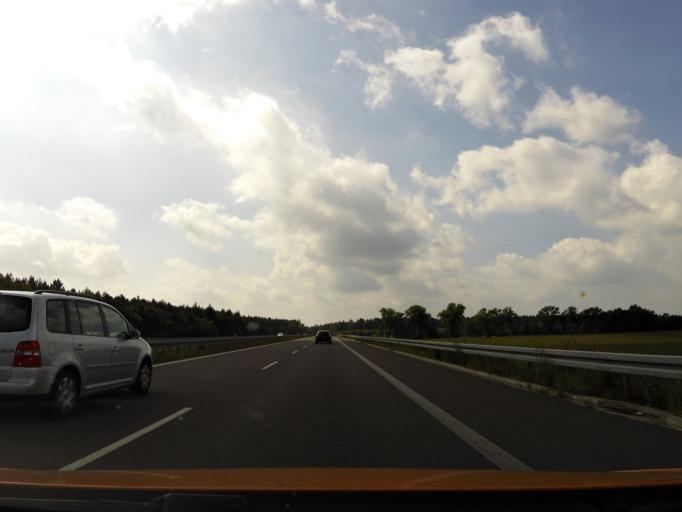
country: PL
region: West Pomeranian Voivodeship
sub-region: Powiat goleniowski
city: Nowogard
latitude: 53.6746
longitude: 15.0810
